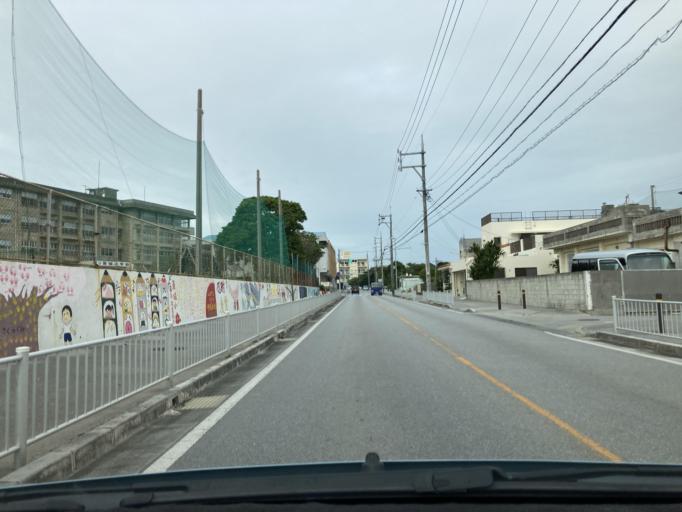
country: JP
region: Okinawa
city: Itoman
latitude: 26.1446
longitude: 127.6903
